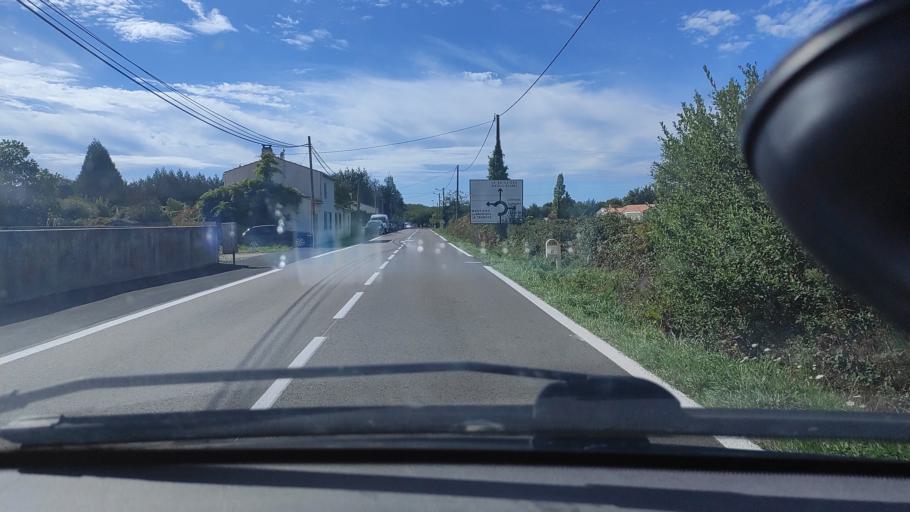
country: FR
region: Pays de la Loire
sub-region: Departement de la Vendee
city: La Boissiere-des-Landes
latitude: 46.5588
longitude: -1.4466
